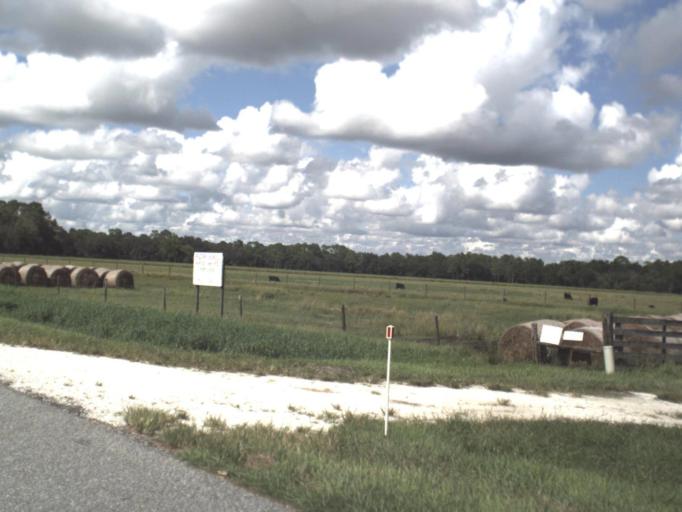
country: US
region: Florida
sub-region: Sarasota County
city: Warm Mineral Springs
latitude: 27.3352
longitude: -82.1361
